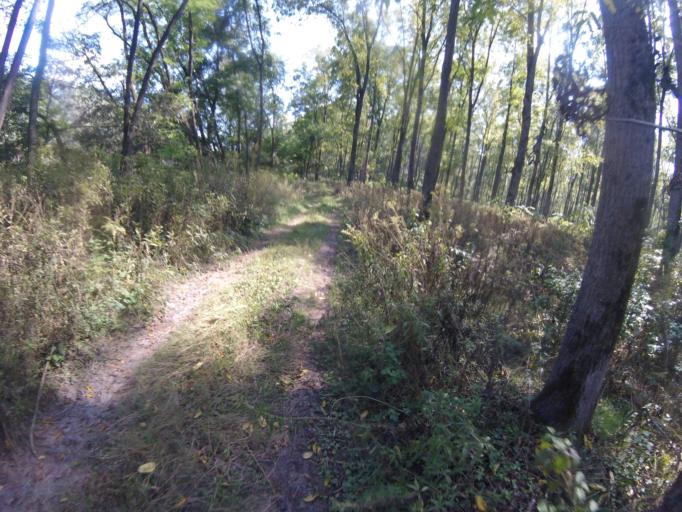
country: HU
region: Bacs-Kiskun
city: Baja
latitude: 46.1996
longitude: 18.8669
